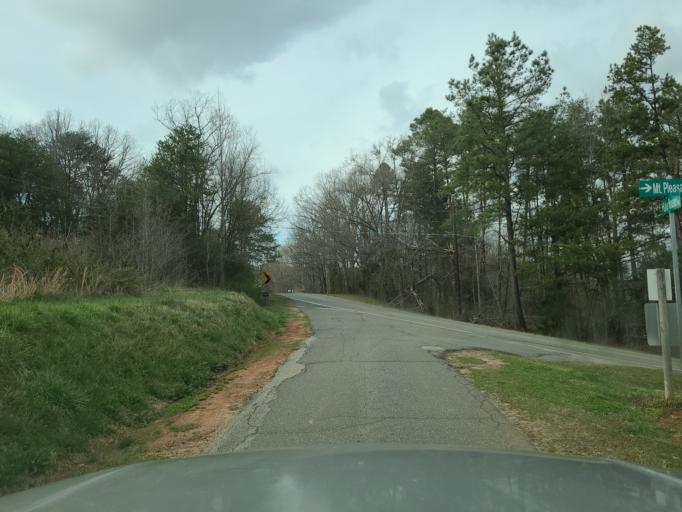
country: US
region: North Carolina
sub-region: Cleveland County
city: Boiling Springs
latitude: 35.2284
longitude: -81.7345
